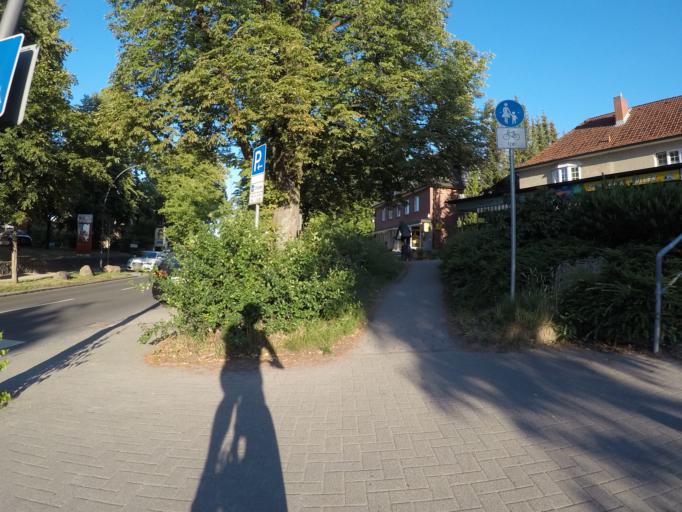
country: DE
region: Hamburg
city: Duvenstedt
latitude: 53.7077
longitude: 10.1087
